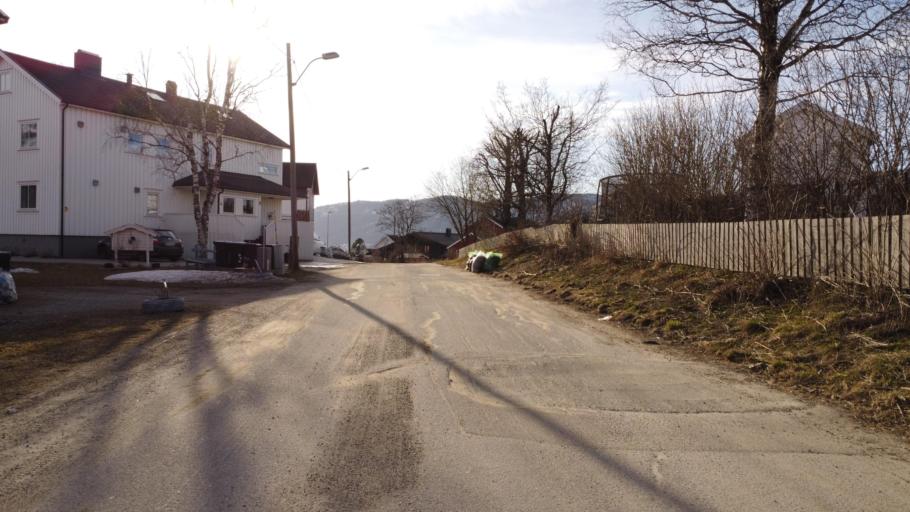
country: NO
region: Nordland
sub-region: Rana
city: Mo i Rana
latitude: 66.3148
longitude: 14.1427
